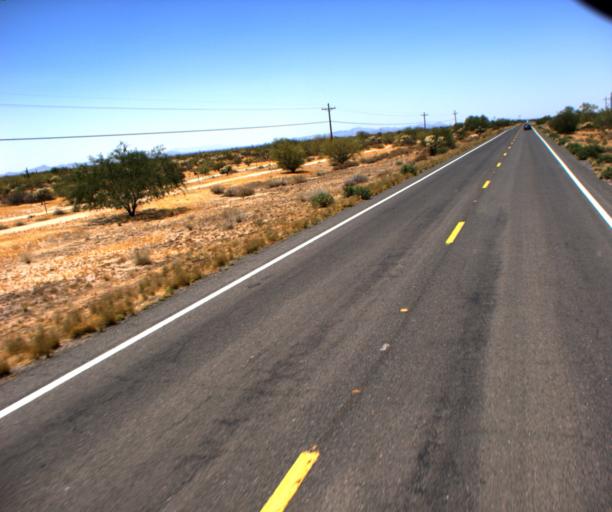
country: US
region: Arizona
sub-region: Pinal County
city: Florence
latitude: 32.9204
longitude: -111.2973
